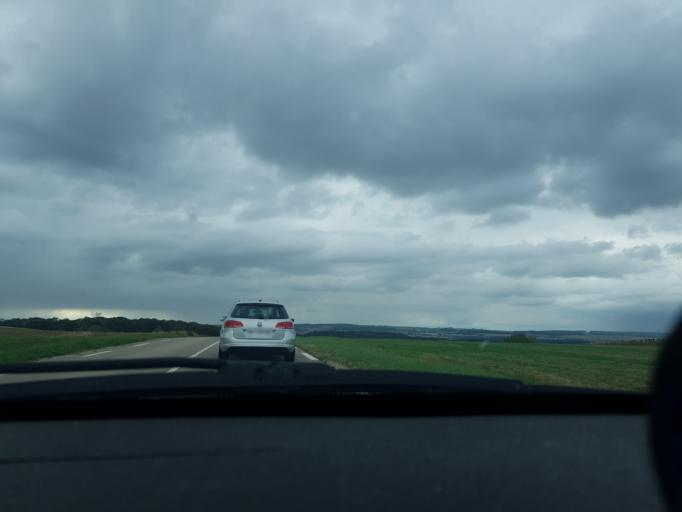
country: FR
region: Lorraine
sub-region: Departement de la Moselle
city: Faulquemont
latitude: 48.9981
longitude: 6.5964
